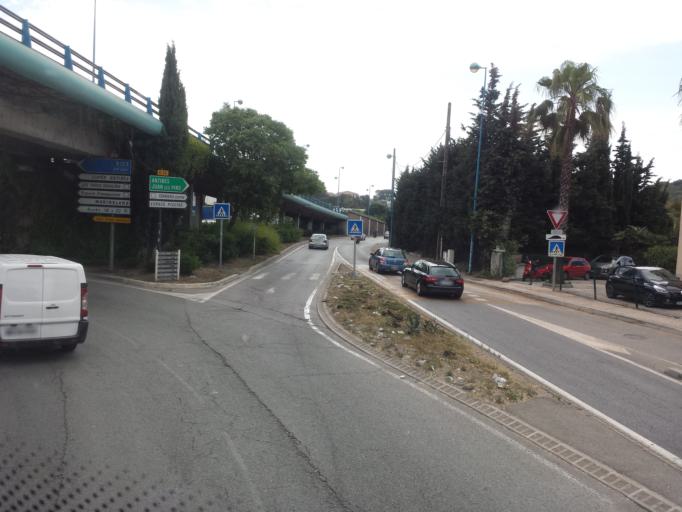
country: FR
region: Provence-Alpes-Cote d'Azur
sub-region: Departement des Alpes-Maritimes
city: Biot
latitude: 43.6016
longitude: 7.0838
